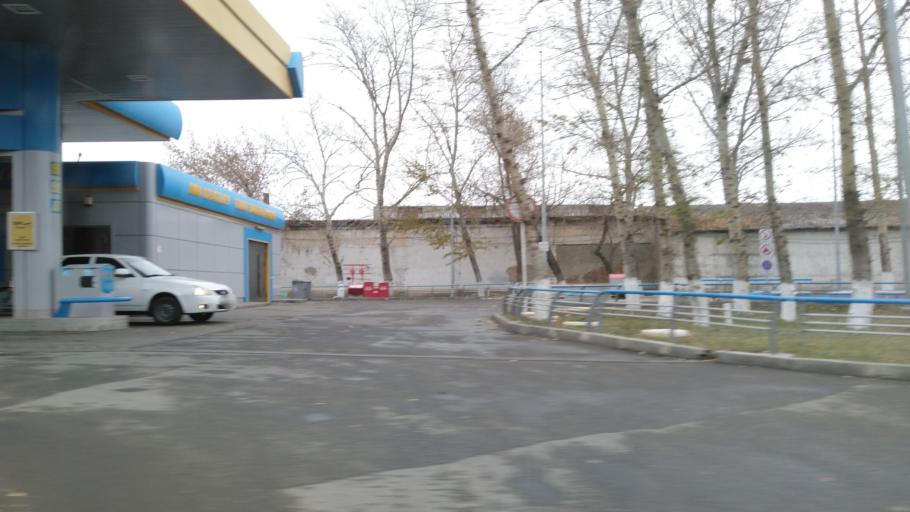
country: KZ
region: Pavlodar
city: Pavlodar
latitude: 52.2783
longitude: 76.9620
